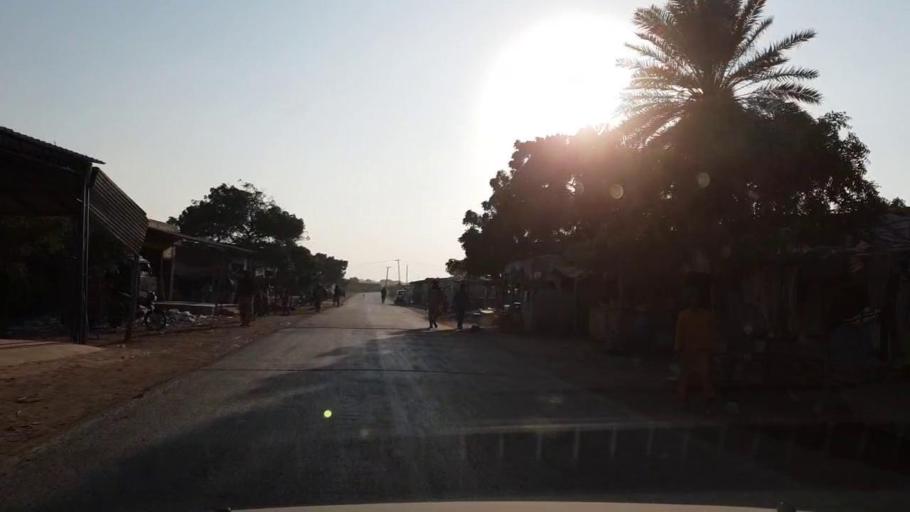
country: PK
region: Sindh
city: Mirpur Batoro
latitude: 24.6886
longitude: 68.1769
